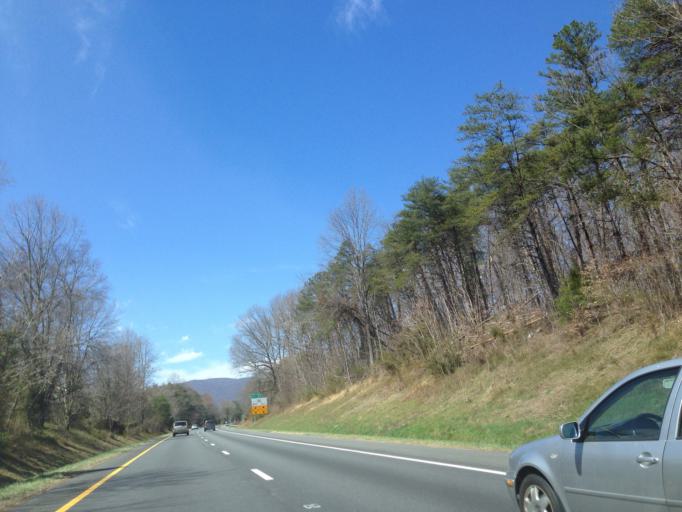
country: US
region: Virginia
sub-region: Albemarle County
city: Crozet
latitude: 38.0405
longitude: -78.7149
